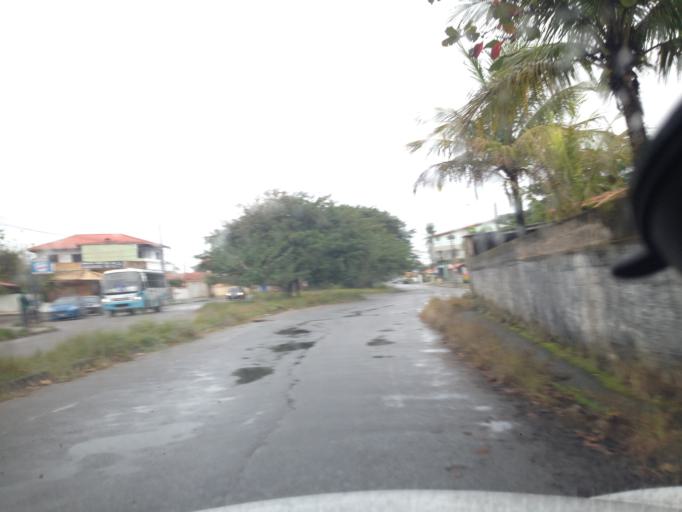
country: BR
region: Sao Paulo
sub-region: Itanhaem
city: Itanhaem
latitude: -24.2297
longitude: -46.8734
